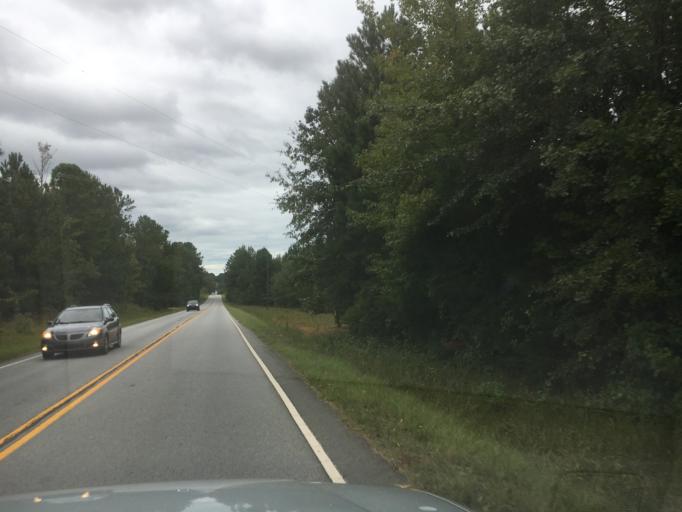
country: US
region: South Carolina
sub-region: McCormick County
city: McCormick
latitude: 34.0625
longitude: -82.2479
